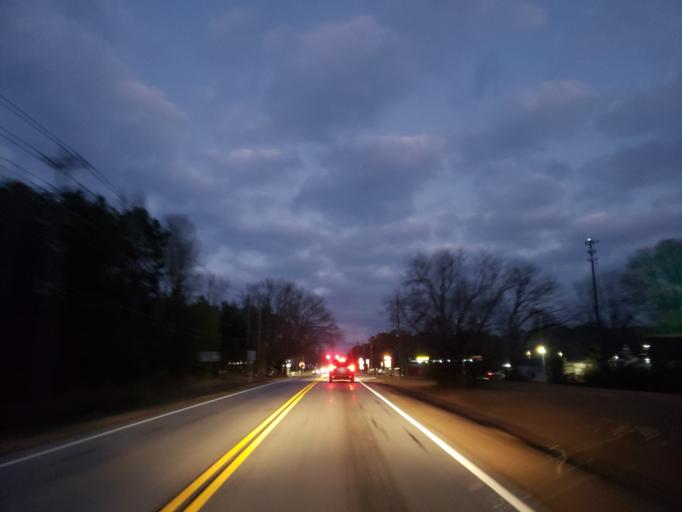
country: US
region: Georgia
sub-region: Carroll County
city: Temple
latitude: 33.8428
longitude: -84.9828
